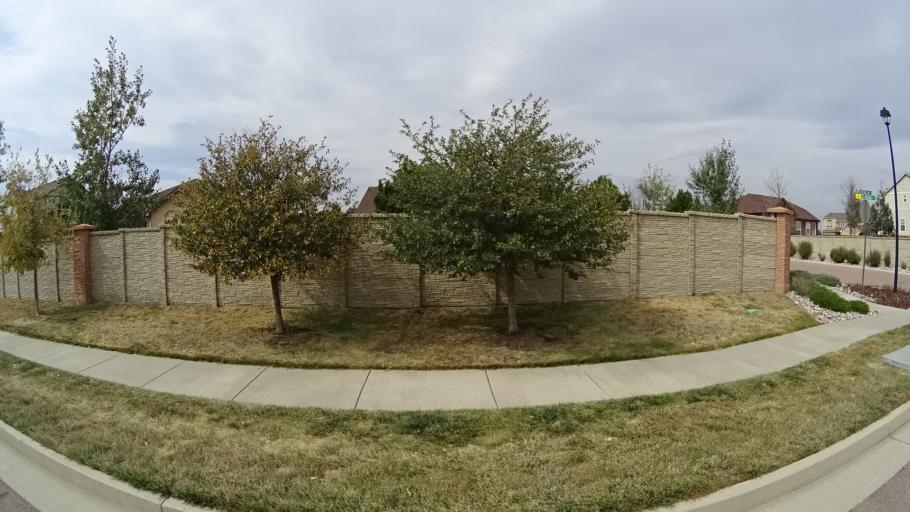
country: US
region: Colorado
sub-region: El Paso County
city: Cimarron Hills
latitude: 38.9250
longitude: -104.6907
